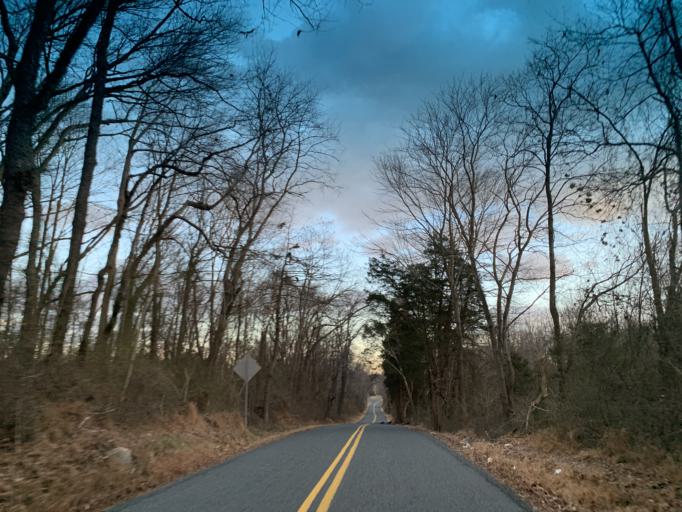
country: US
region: Maryland
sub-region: Harford County
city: South Bel Air
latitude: 39.6510
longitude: -76.2897
